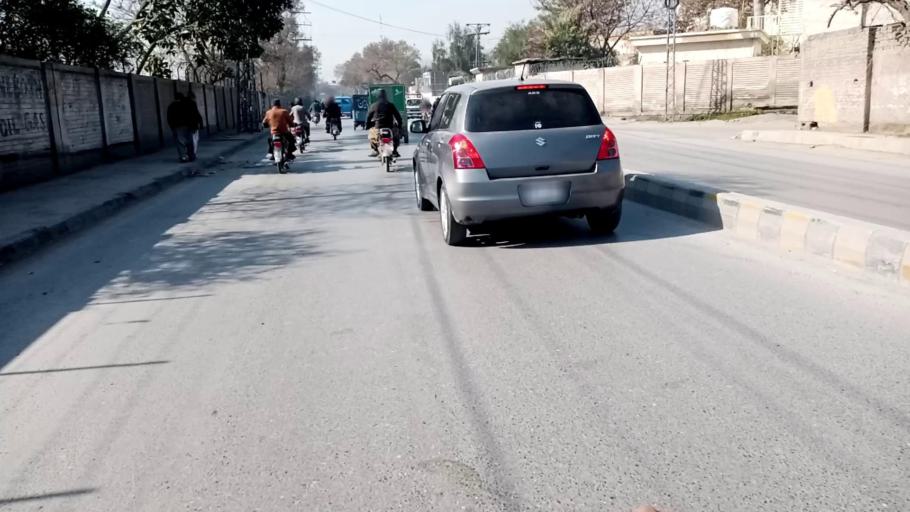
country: PK
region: Khyber Pakhtunkhwa
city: Peshawar
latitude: 34.0064
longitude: 71.5555
